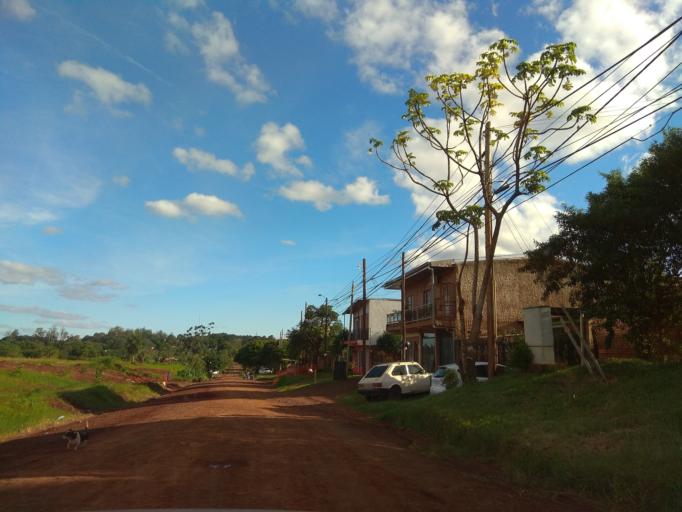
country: AR
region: Misiones
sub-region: Departamento de Capital
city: Posadas
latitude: -27.3923
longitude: -55.9276
